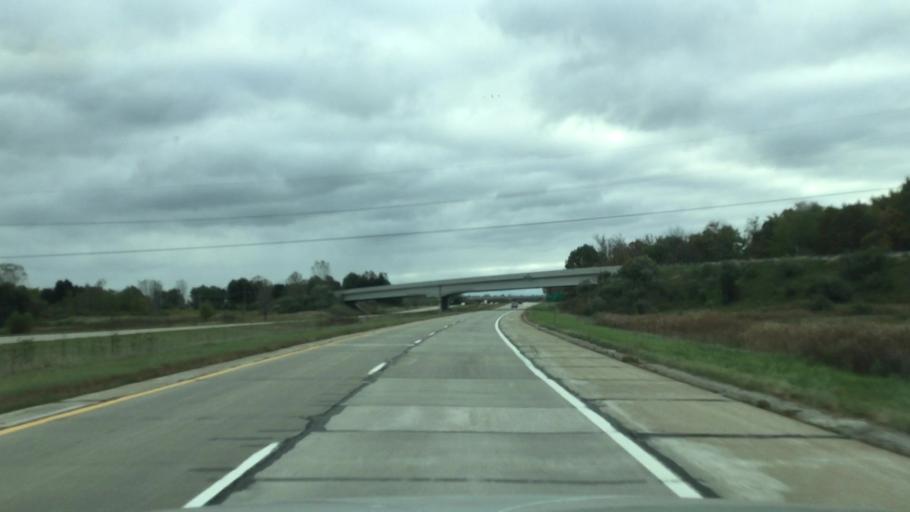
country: US
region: Michigan
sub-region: Saint Clair County
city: Capac
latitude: 42.9854
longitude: -82.8551
